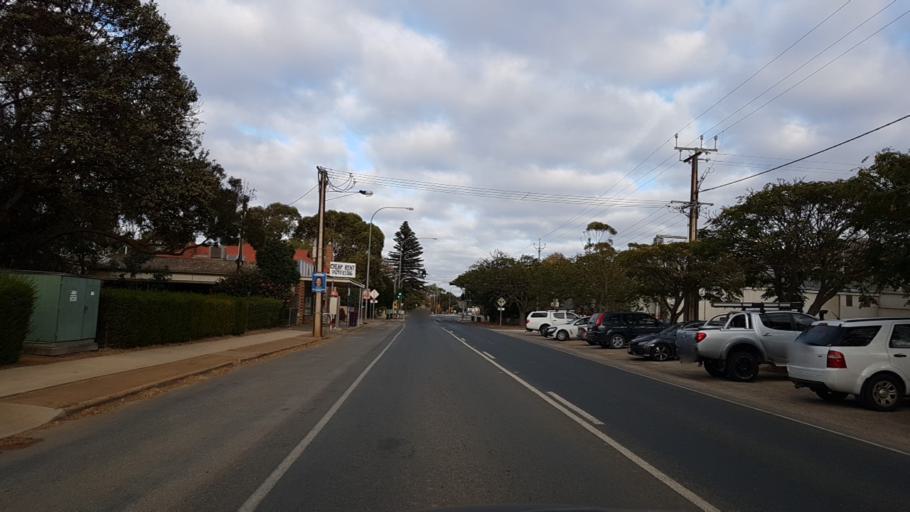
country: AU
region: South Australia
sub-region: Alexandrina
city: Strathalbyn
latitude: -35.2576
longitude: 138.9002
